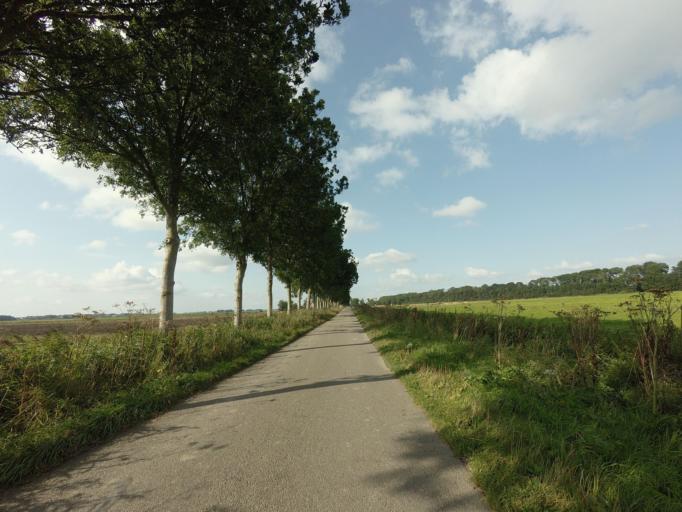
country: NL
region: Flevoland
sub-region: Gemeente Noordoostpolder
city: Ens
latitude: 52.6186
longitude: 5.7672
